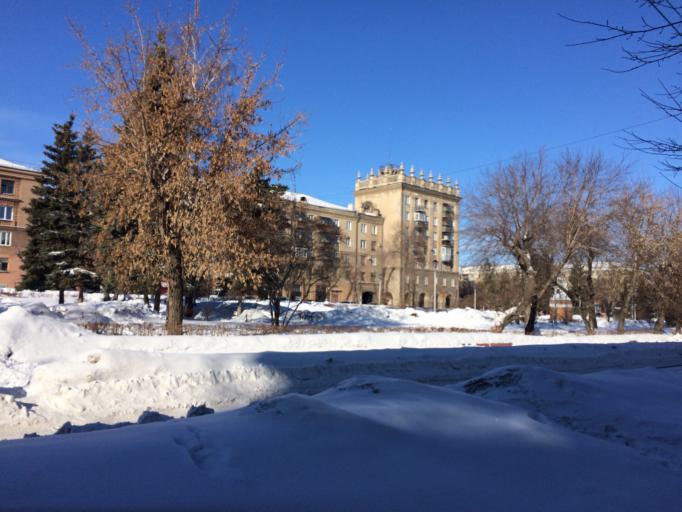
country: RU
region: Chelyabinsk
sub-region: Gorod Magnitogorsk
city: Magnitogorsk
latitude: 53.4209
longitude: 58.9966
